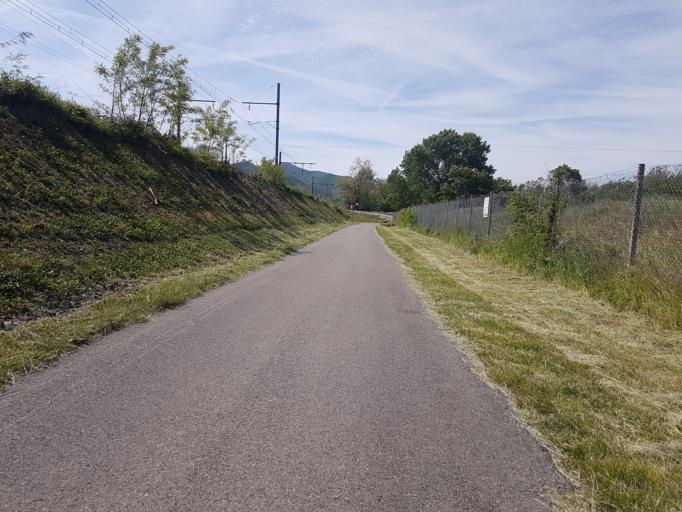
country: FR
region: Rhone-Alpes
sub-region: Departement de l'Ardeche
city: Le Pouzin
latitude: 44.7328
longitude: 4.7468
